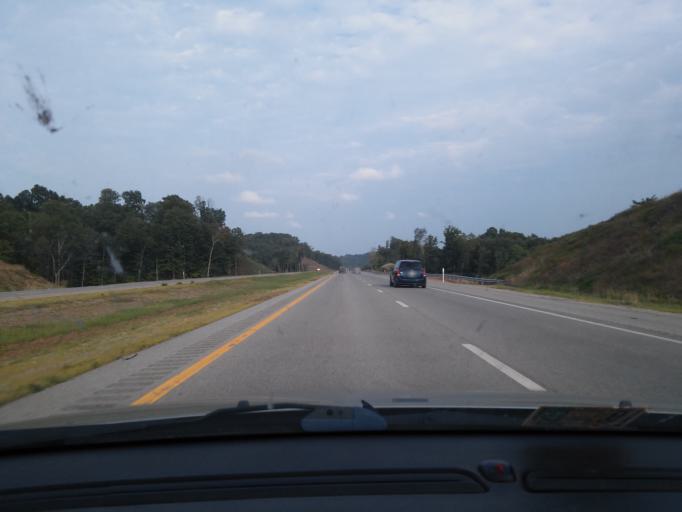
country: US
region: West Virginia
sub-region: Mason County
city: Point Pleasant
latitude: 38.7862
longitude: -82.0834
